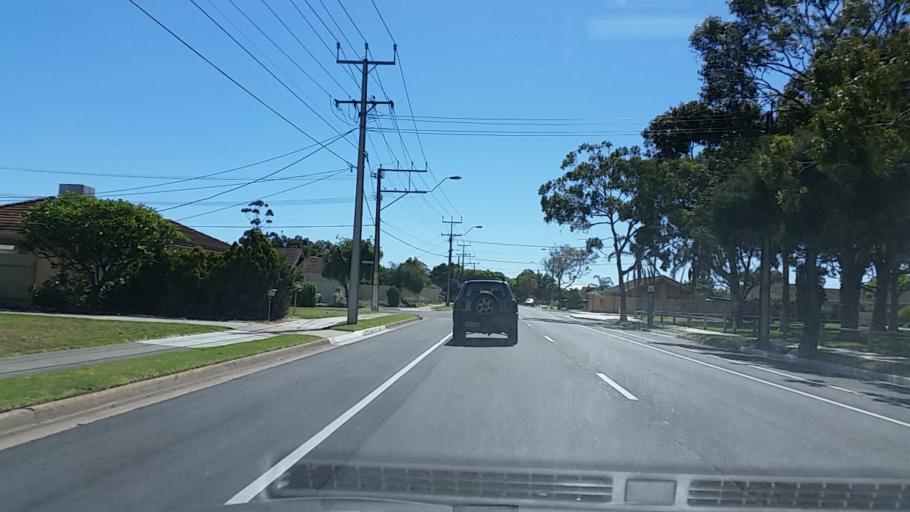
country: AU
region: South Australia
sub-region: Charles Sturt
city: Findon
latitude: -34.9122
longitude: 138.5375
